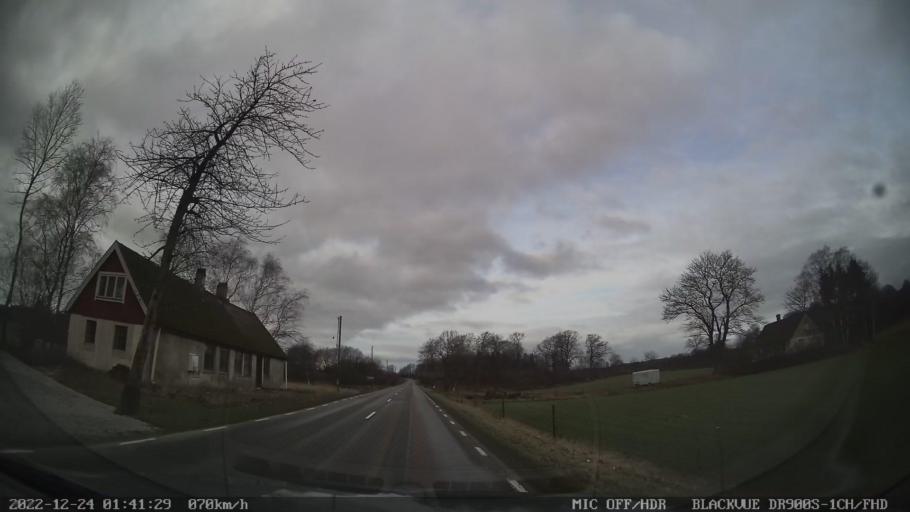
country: SE
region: Skane
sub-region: Tomelilla Kommun
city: Tomelilla
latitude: 55.5944
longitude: 14.0896
